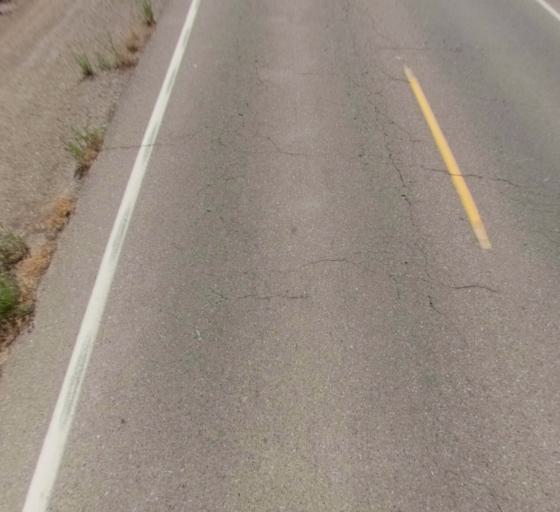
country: US
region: California
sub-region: Madera County
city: Parkwood
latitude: 36.8480
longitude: -120.1300
